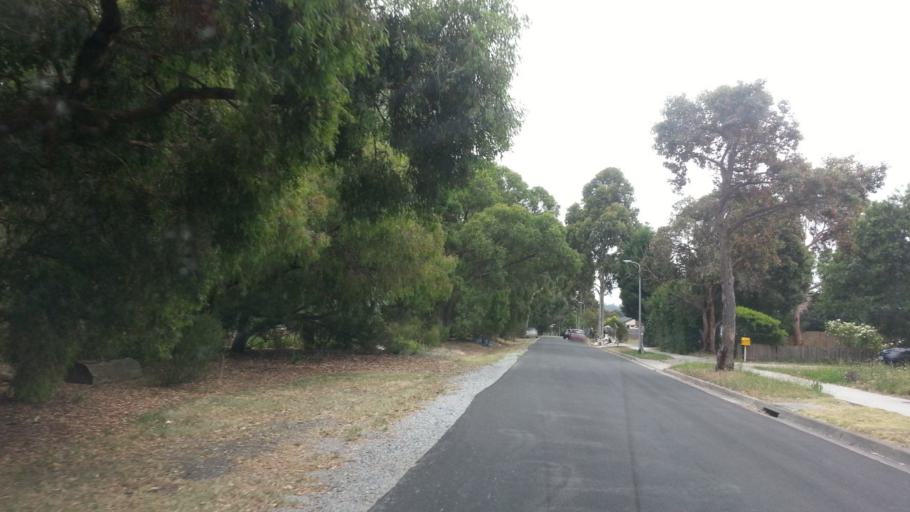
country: AU
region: Victoria
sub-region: Knox
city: Scoresby
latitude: -37.9089
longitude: 145.2476
